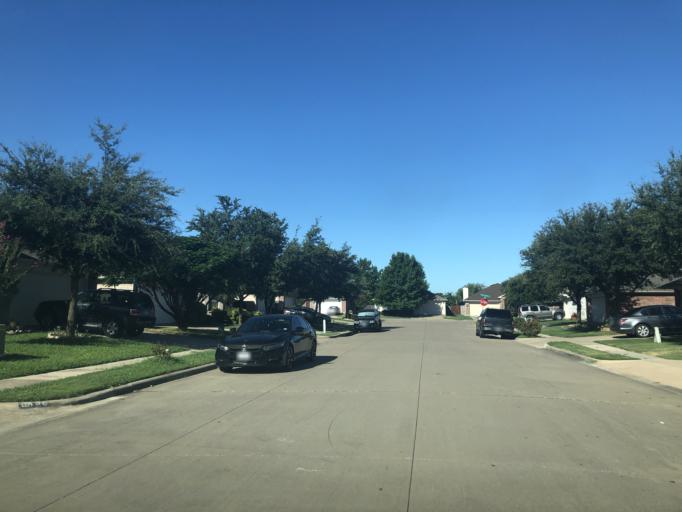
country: US
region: Texas
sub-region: Dallas County
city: Duncanville
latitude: 32.6571
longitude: -96.9766
